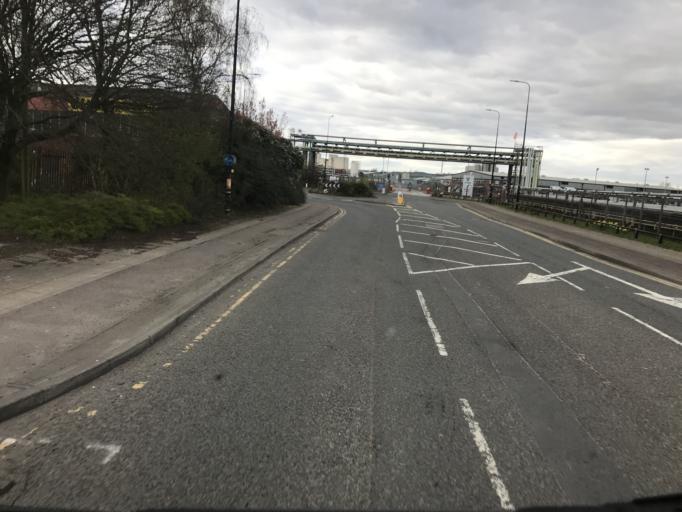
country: GB
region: England
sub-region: Trafford
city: Trafford Park
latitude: 53.4727
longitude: -2.3100
